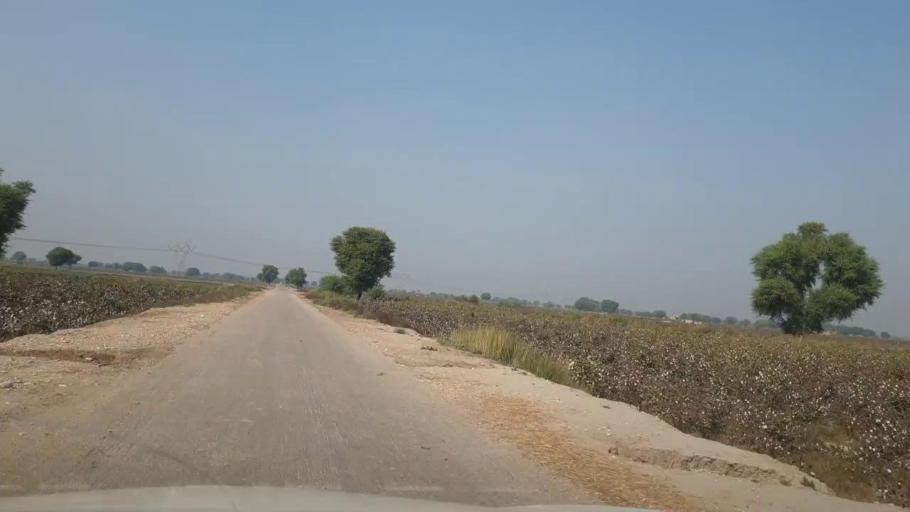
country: PK
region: Sindh
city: Bhan
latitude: 26.5309
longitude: 67.7532
